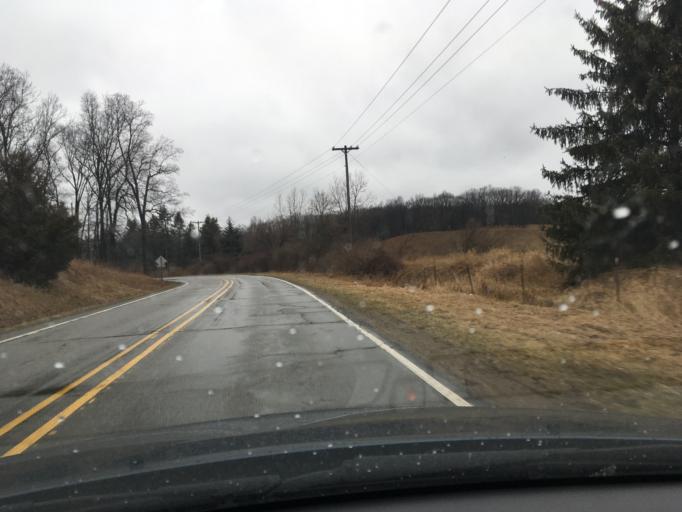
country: US
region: Michigan
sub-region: Jackson County
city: Grass Lake
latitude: 42.3118
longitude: -84.1504
